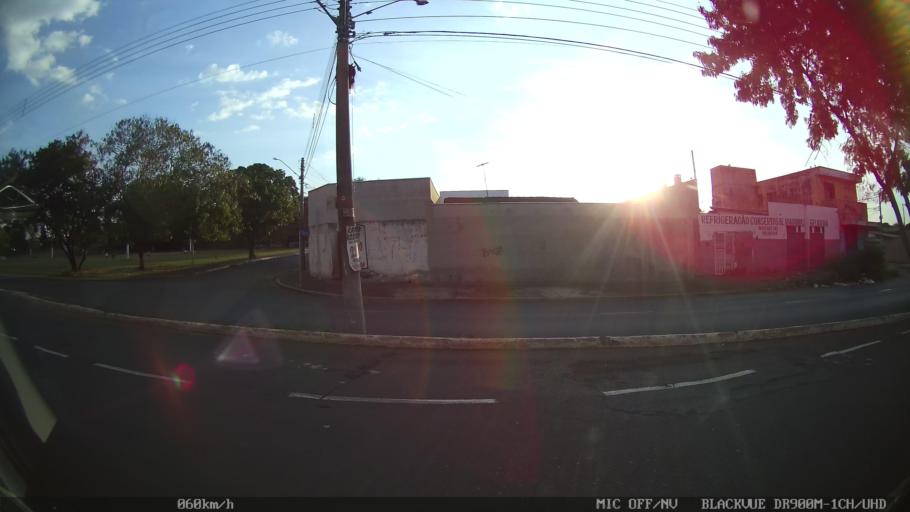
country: BR
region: Sao Paulo
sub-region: Ribeirao Preto
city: Ribeirao Preto
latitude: -21.1300
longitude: -47.8039
